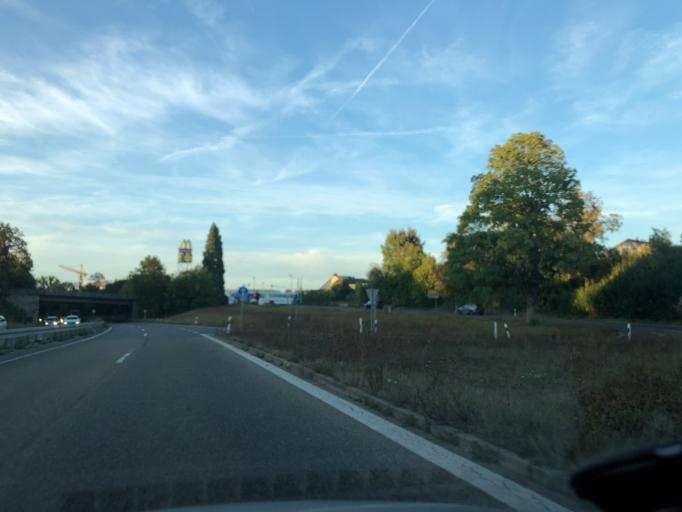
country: DE
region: Baden-Wuerttemberg
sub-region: Regierungsbezirk Stuttgart
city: Kornwestheim
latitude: 48.8651
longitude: 9.1972
